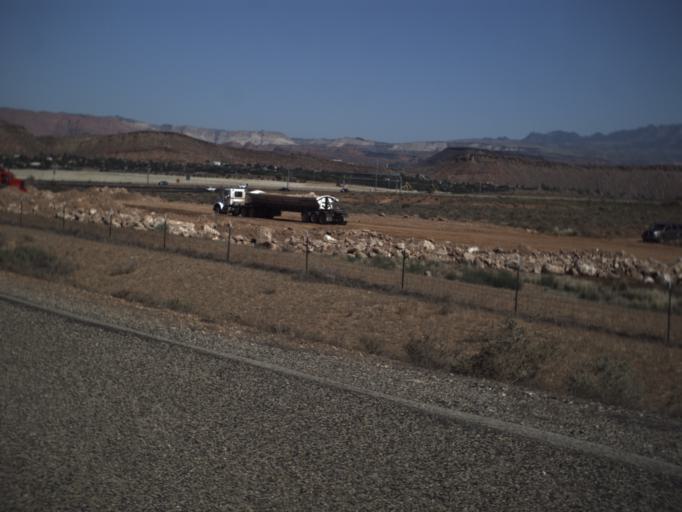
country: US
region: Utah
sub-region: Washington County
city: Saint George
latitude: 37.0259
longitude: -113.6022
